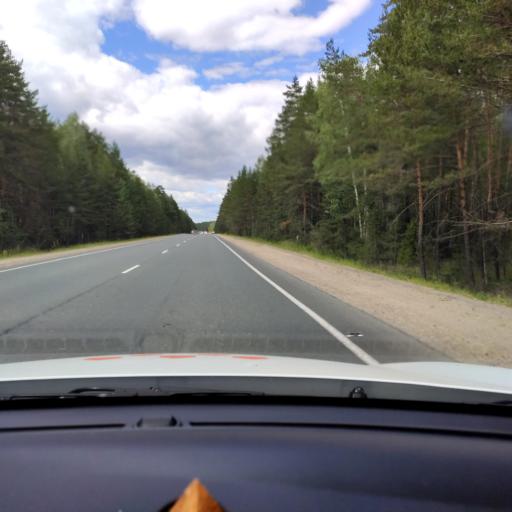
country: RU
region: Mariy-El
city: Pomary
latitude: 56.0492
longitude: 48.3752
